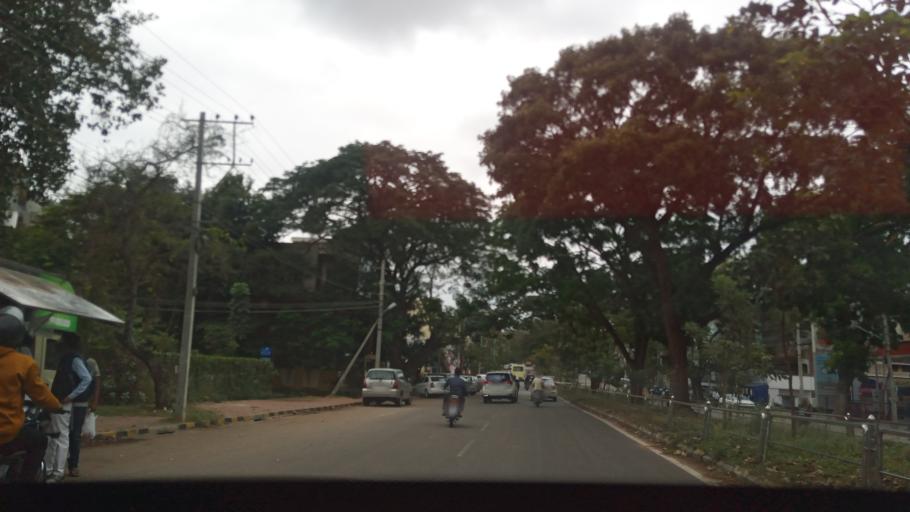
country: IN
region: Karnataka
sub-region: Mysore
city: Mysore
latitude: 12.2979
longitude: 76.6259
